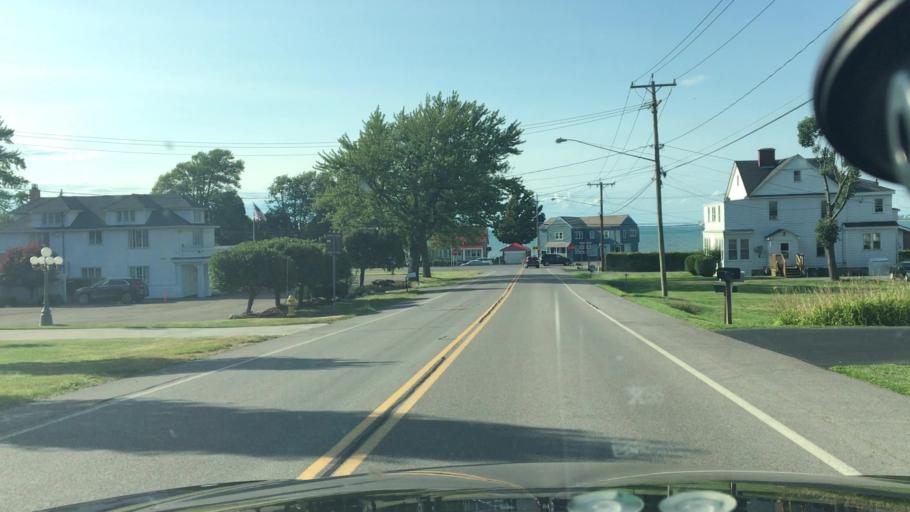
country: US
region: New York
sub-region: Erie County
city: Wanakah
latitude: 42.7689
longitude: -78.8667
